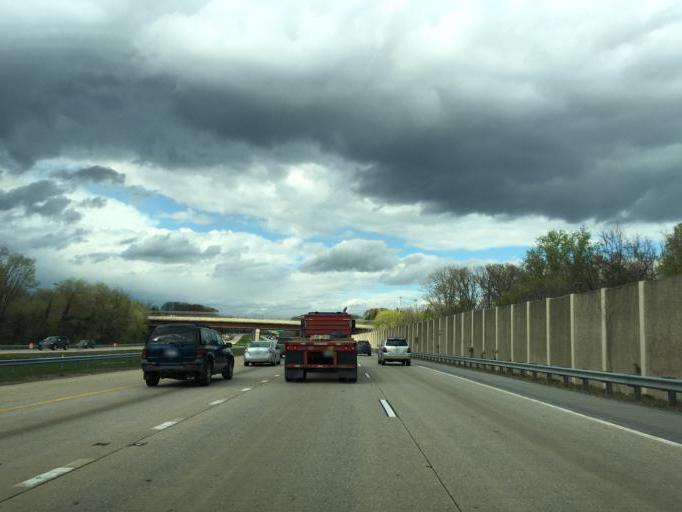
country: US
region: Maryland
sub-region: Anne Arundel County
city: Ferndale
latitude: 39.1830
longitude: -76.6324
